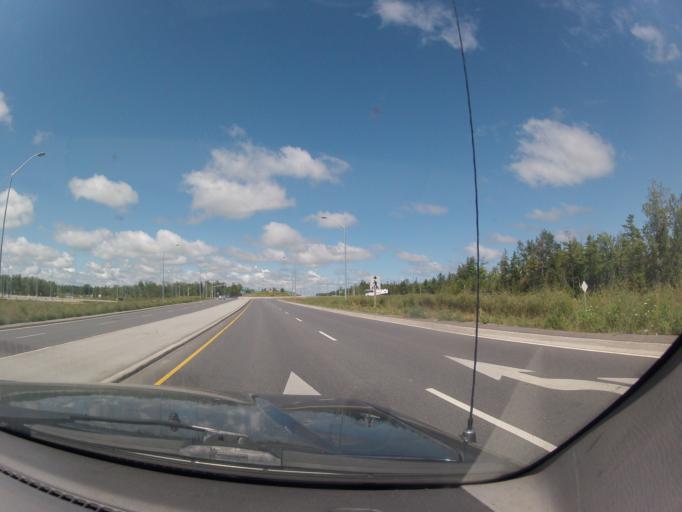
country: CA
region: Ontario
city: Collingwood
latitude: 44.4614
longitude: -80.1113
